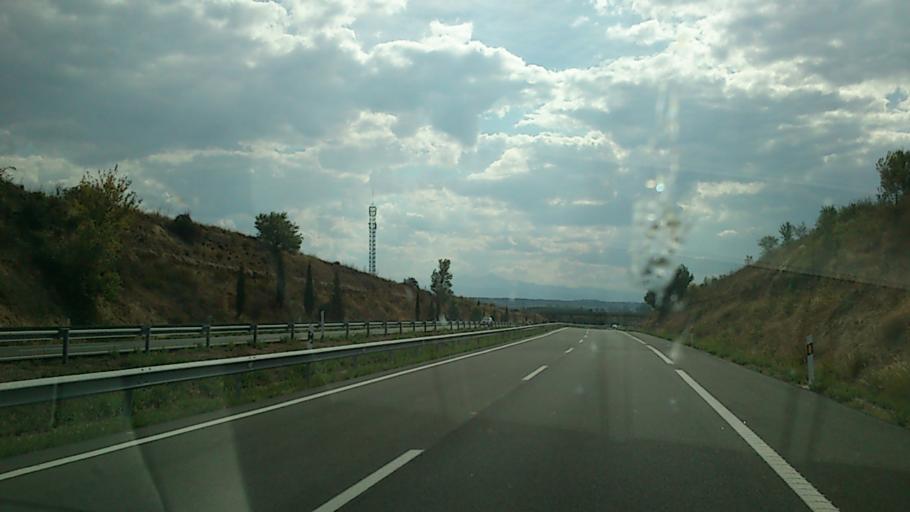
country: ES
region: La Rioja
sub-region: Provincia de La Rioja
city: Haro
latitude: 42.5887
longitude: -2.8659
